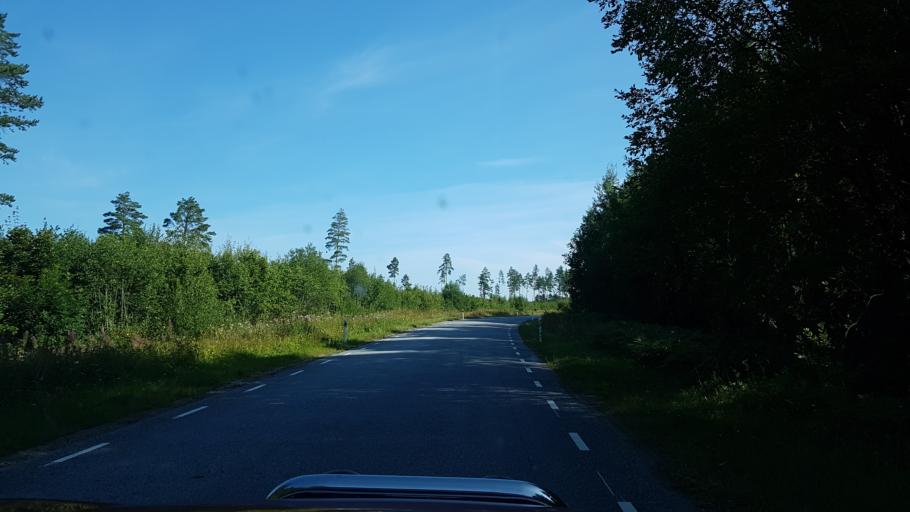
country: EE
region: Harju
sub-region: Raasiku vald
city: Raasiku
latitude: 59.2866
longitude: 25.1629
